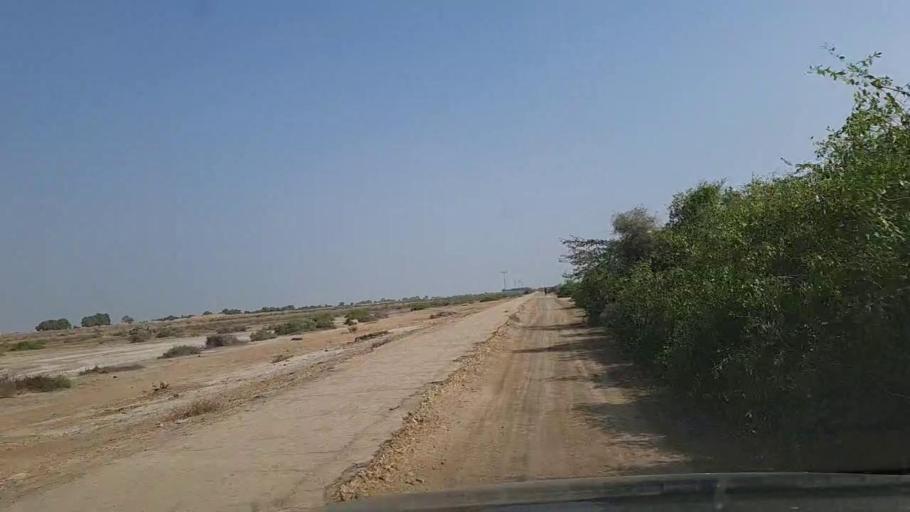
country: PK
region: Sindh
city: Gharo
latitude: 24.7413
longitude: 67.6461
